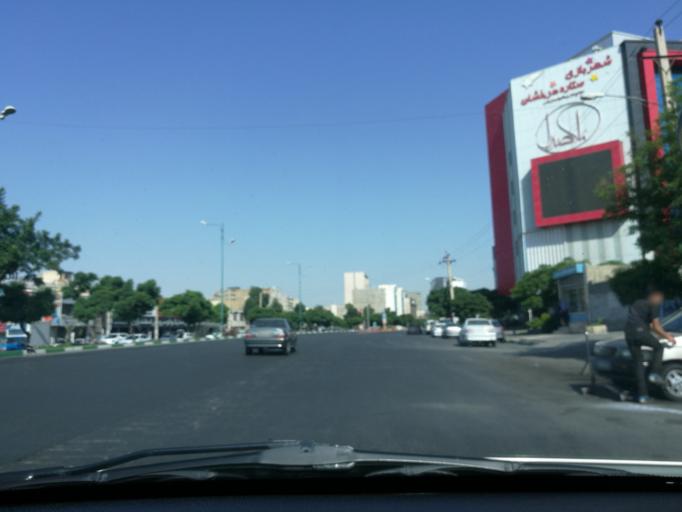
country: IR
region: Alborz
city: Karaj
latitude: 35.8426
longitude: 50.9789
